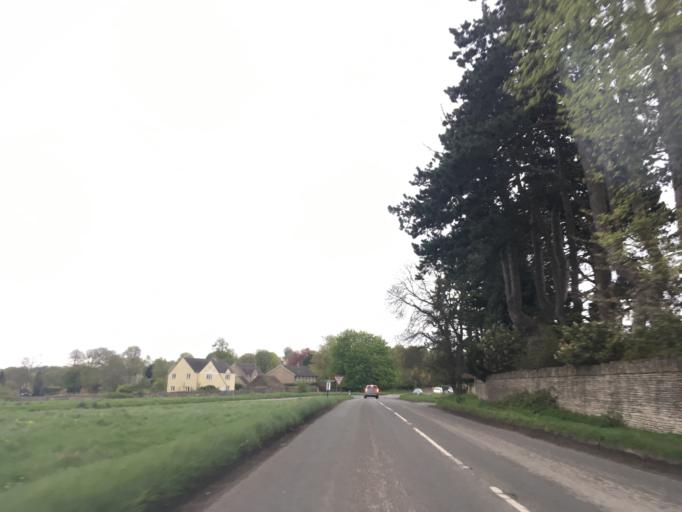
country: GB
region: England
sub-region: Gloucestershire
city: Stroud
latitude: 51.7251
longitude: -2.2137
